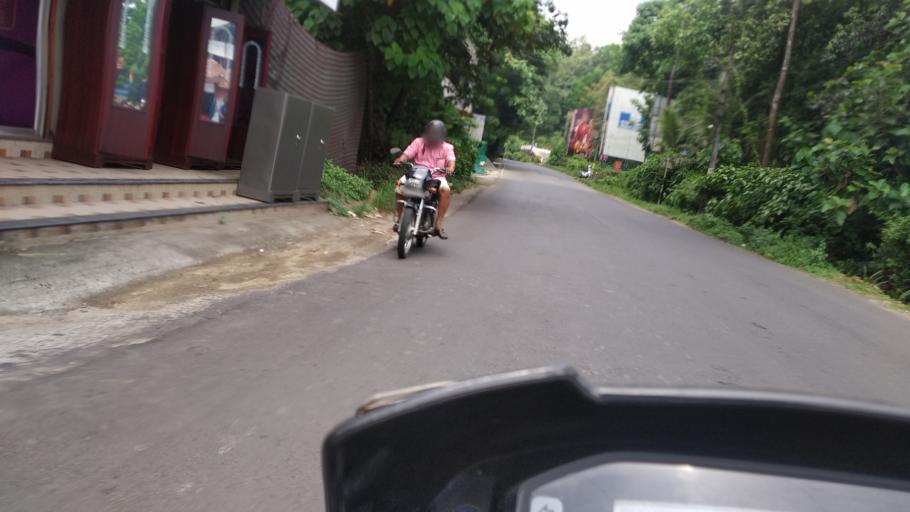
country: IN
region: Kerala
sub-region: Ernakulam
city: Perumpavur
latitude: 10.1014
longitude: 76.5419
